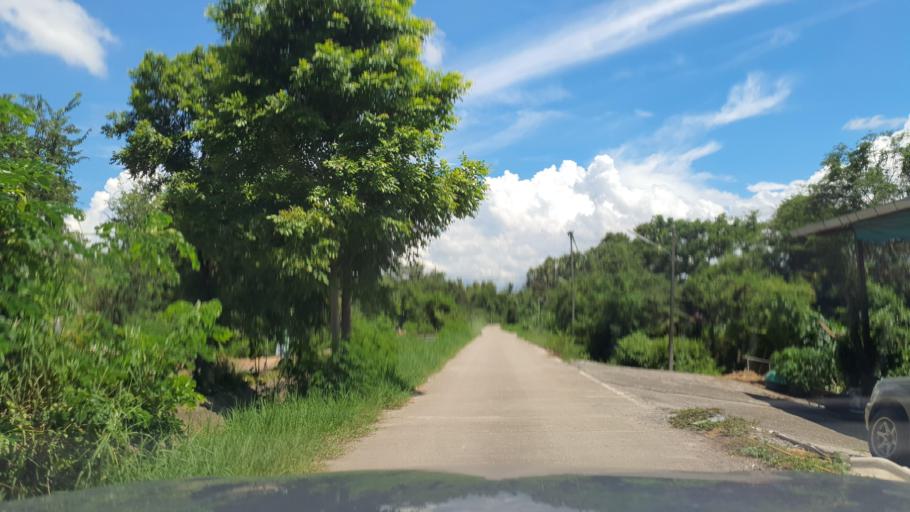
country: TH
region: Chiang Mai
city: San Kamphaeng
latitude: 18.7331
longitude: 99.1183
